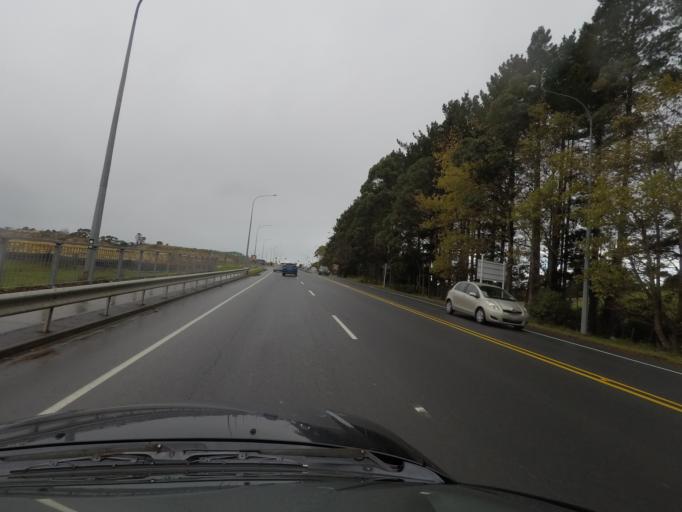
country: NZ
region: Auckland
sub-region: Auckland
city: Rothesay Bay
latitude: -36.7327
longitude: 174.7205
